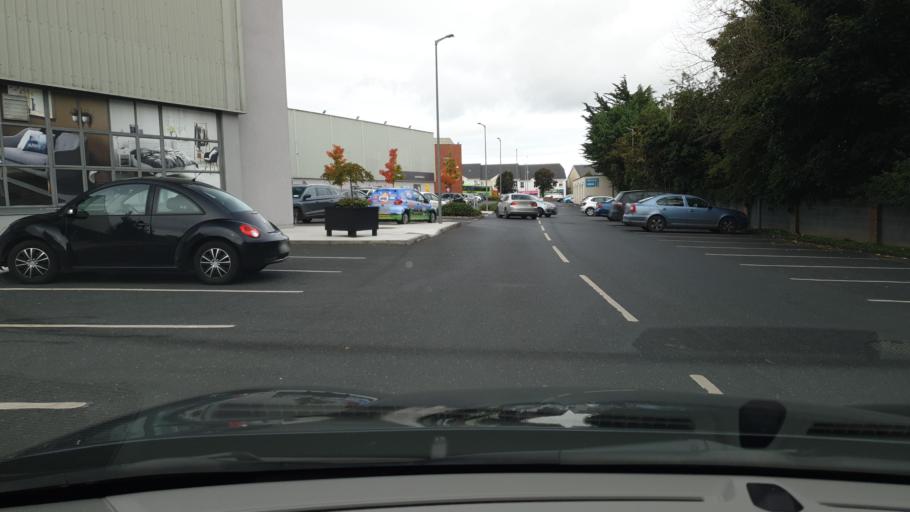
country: IE
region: Leinster
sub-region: Laois
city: Portlaoise
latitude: 53.0316
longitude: -7.2952
